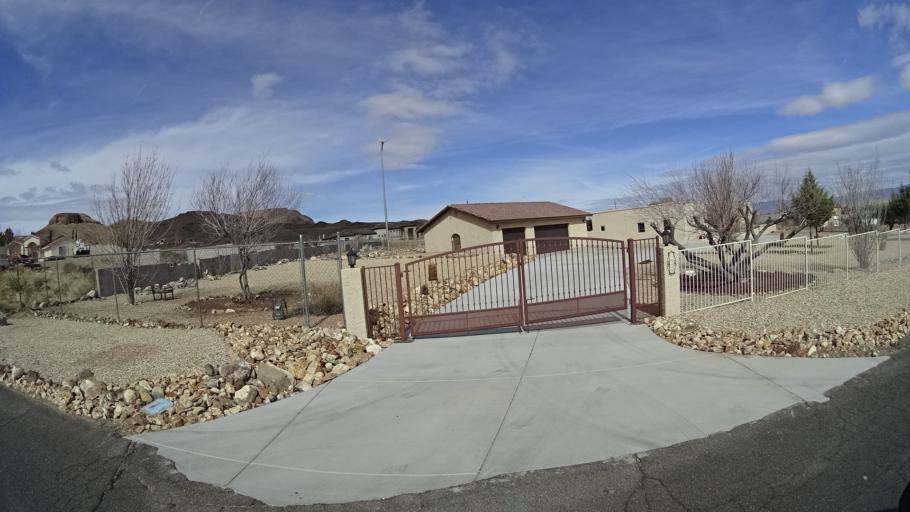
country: US
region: Arizona
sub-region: Mohave County
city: New Kingman-Butler
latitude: 35.2358
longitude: -114.0513
